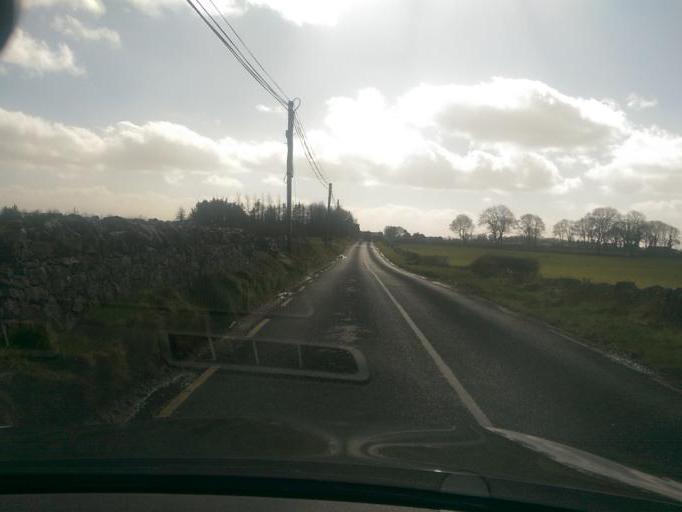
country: IE
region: Connaught
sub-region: County Galway
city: Athenry
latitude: 53.3571
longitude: -8.7050
